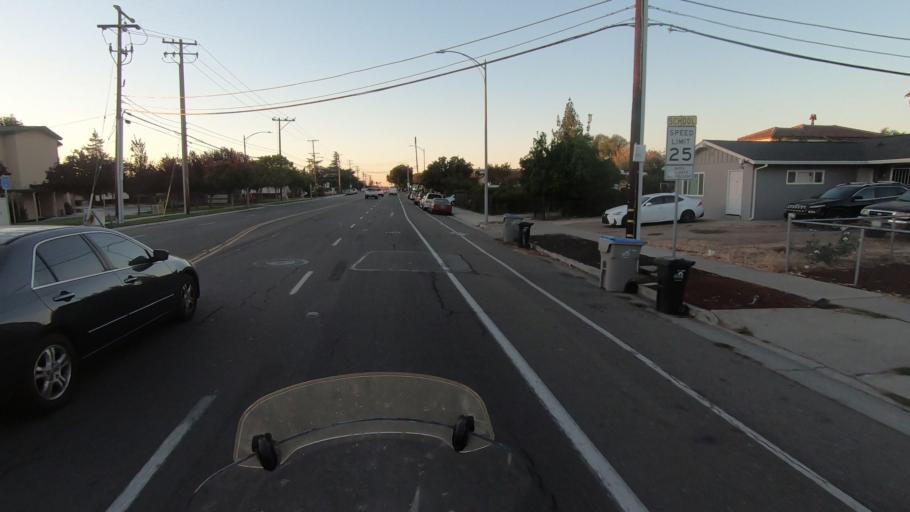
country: US
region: California
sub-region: Santa Clara County
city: Alum Rock
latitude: 37.3483
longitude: -121.8119
